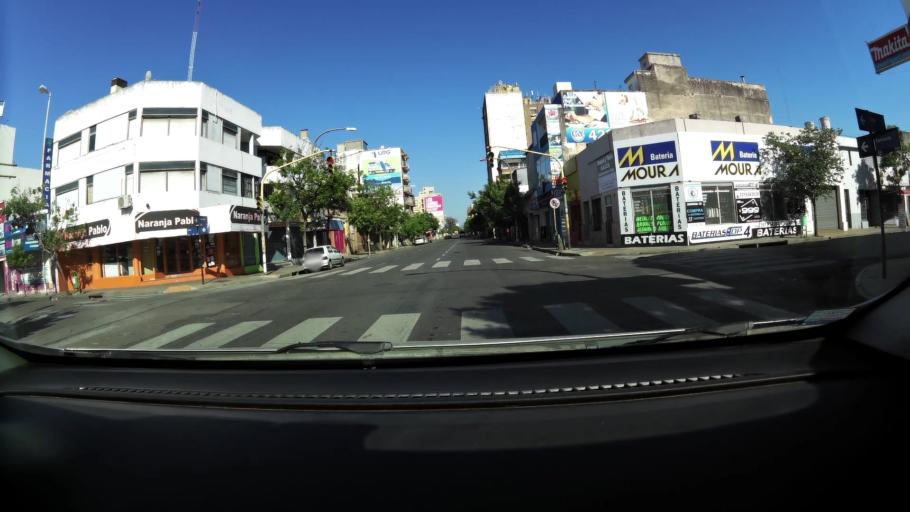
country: AR
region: Cordoba
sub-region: Departamento de Capital
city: Cordoba
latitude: -31.4116
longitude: -64.1763
